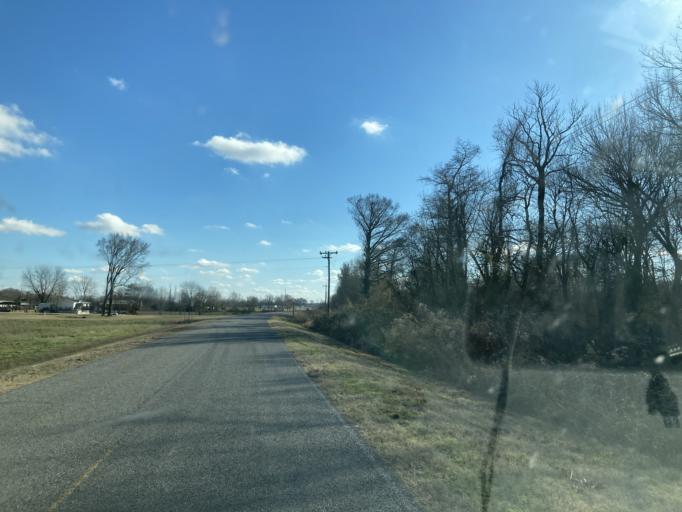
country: US
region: Mississippi
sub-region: Yazoo County
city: Yazoo City
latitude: 32.9357
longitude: -90.4739
